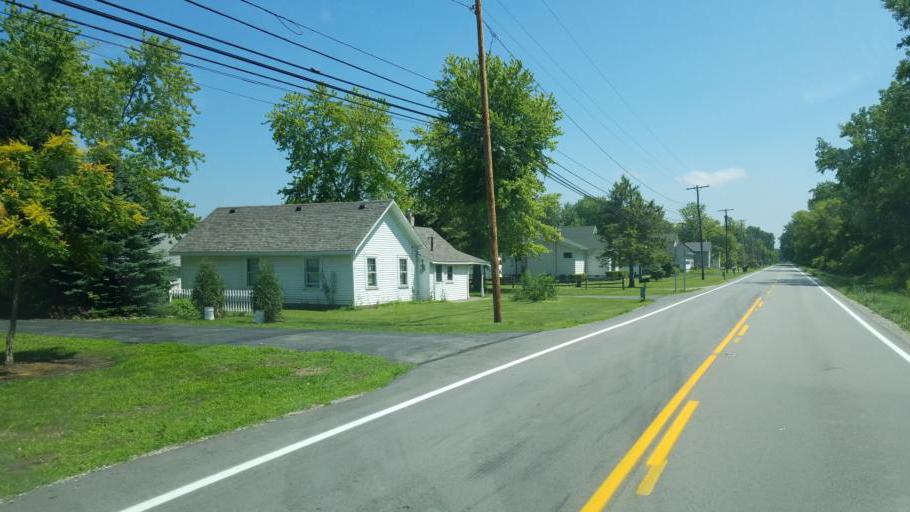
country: US
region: Ohio
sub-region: Erie County
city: Sandusky
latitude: 41.4159
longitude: -82.8160
